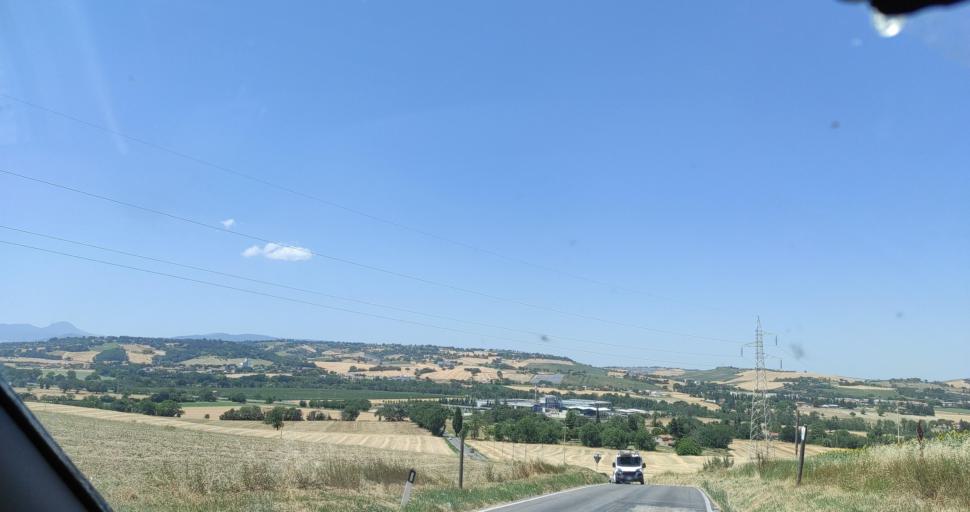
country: IT
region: The Marches
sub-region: Provincia di Macerata
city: Casette Verdini
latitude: 43.2298
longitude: 13.3962
